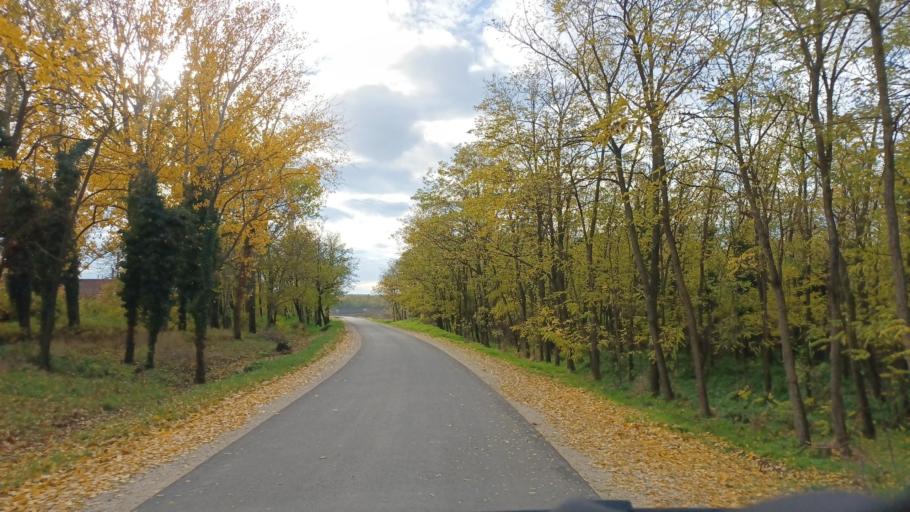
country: HU
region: Fejer
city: Cece
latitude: 46.7149
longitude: 18.6051
